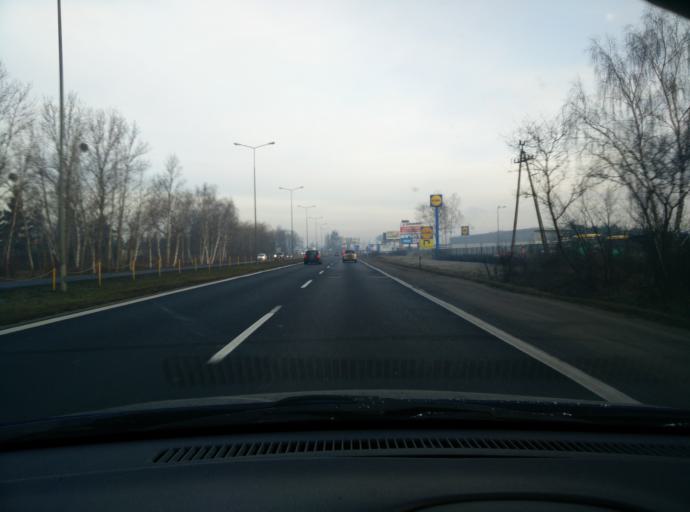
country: PL
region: Greater Poland Voivodeship
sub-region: Powiat poznanski
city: Daszewice
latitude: 52.3652
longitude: 16.9926
